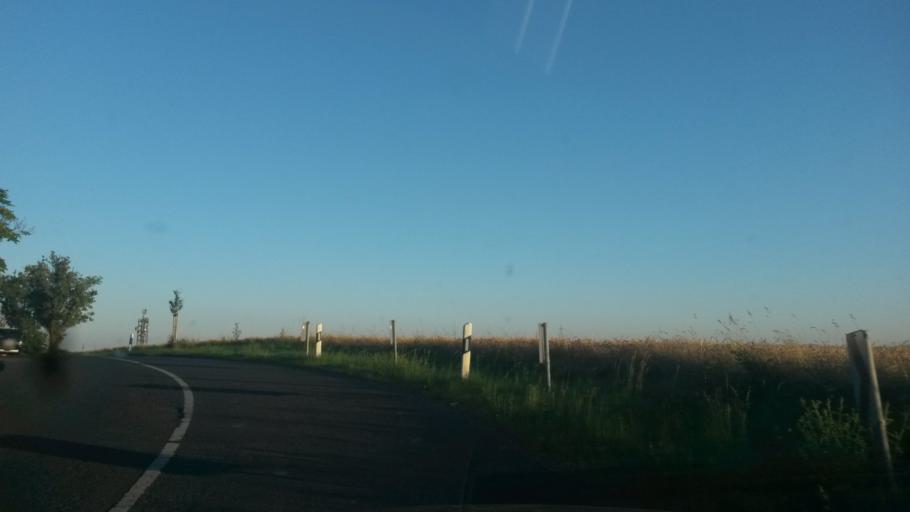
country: DE
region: Bavaria
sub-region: Regierungsbezirk Unterfranken
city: Wuerzburg
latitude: 49.8143
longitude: 9.9394
